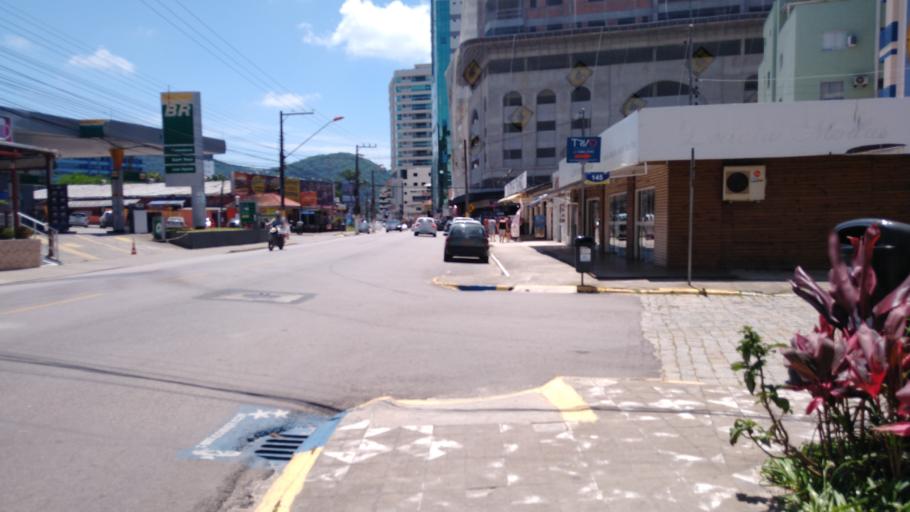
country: BR
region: Santa Catarina
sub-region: Itapema
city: Itapema
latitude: -27.0997
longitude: -48.6156
